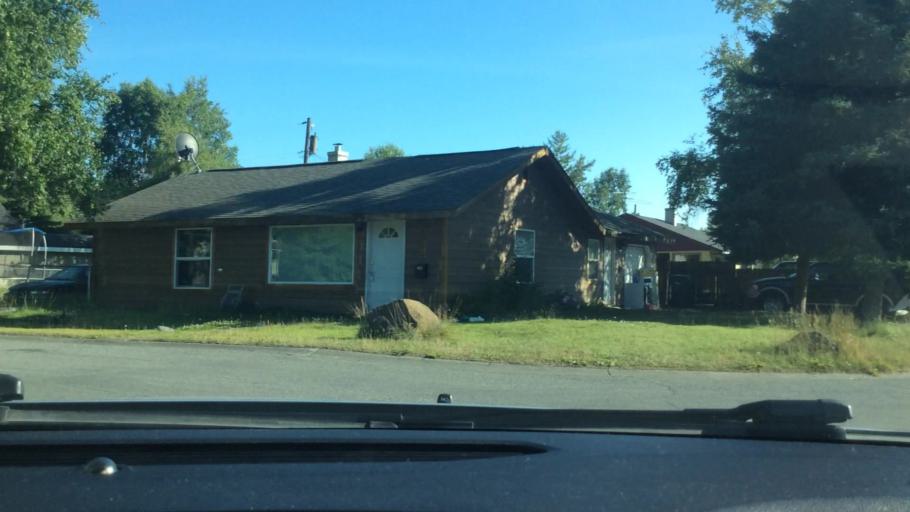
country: US
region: Alaska
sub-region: Anchorage Municipality
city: Anchorage
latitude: 61.2051
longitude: -149.7717
